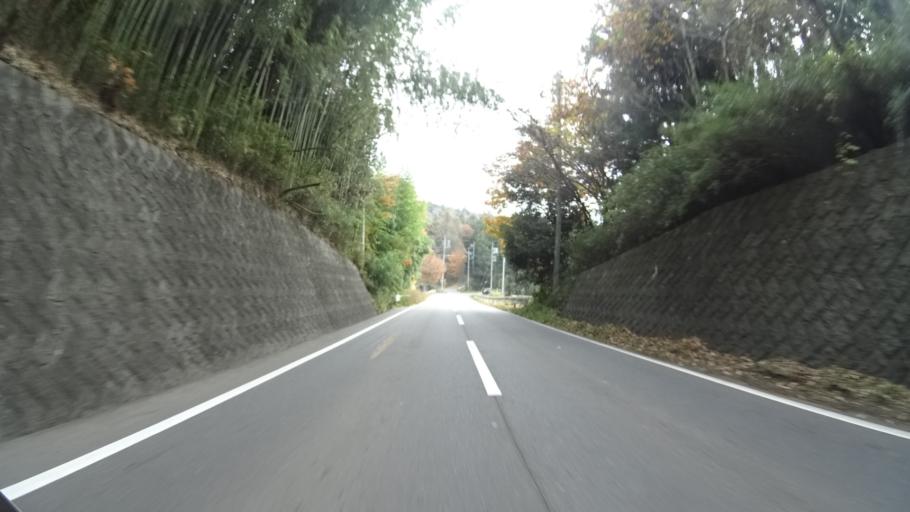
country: JP
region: Gunma
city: Shibukawa
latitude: 36.5133
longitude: 139.0789
